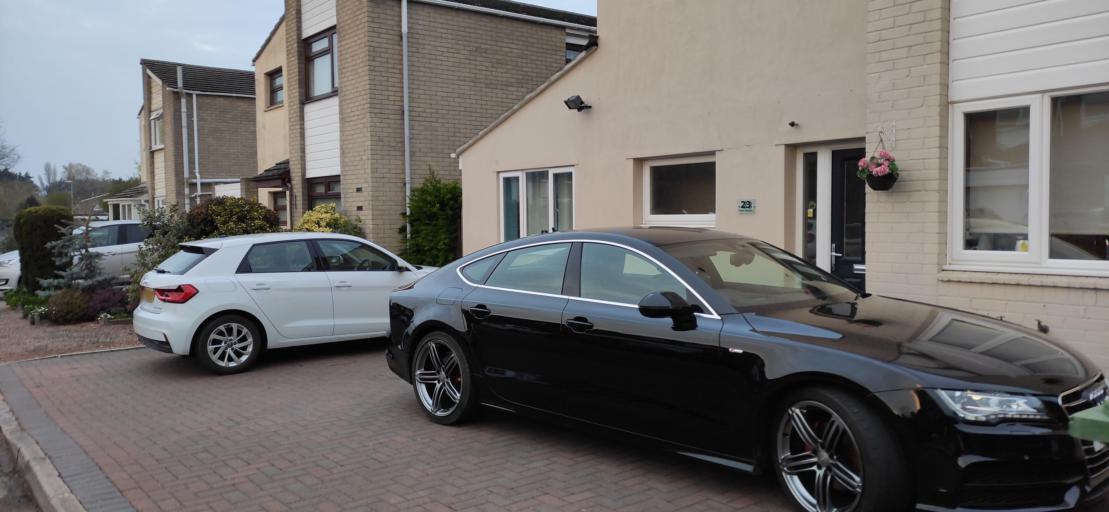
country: GB
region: England
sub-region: Cambridgeshire
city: Swavesey
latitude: 52.2534
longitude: 0.0228
